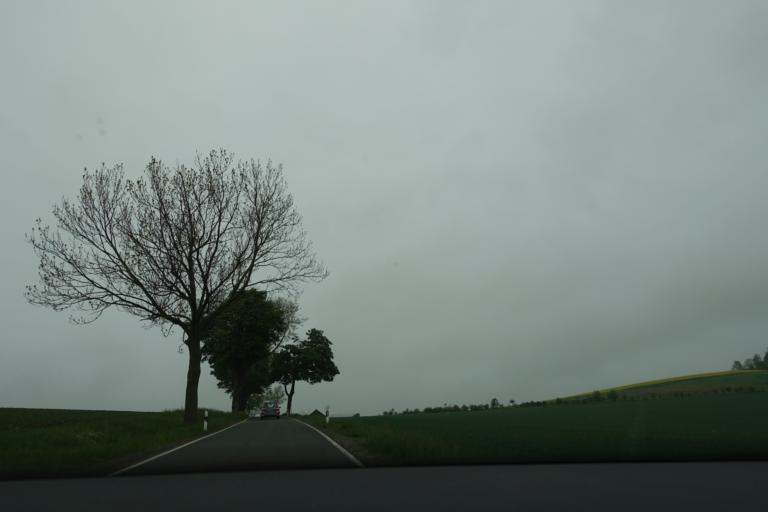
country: DE
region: Saxony
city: Grosshartmannsdorf
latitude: 50.8156
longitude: 13.2975
